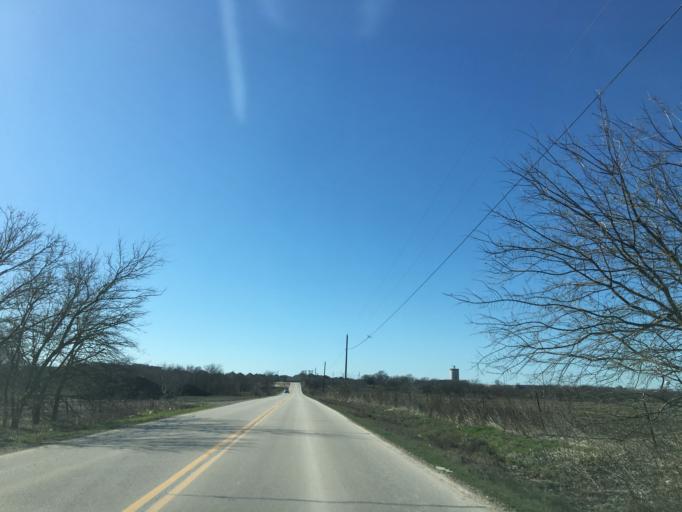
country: US
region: Texas
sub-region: Collin County
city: Prosper
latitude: 33.2317
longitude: -96.8394
